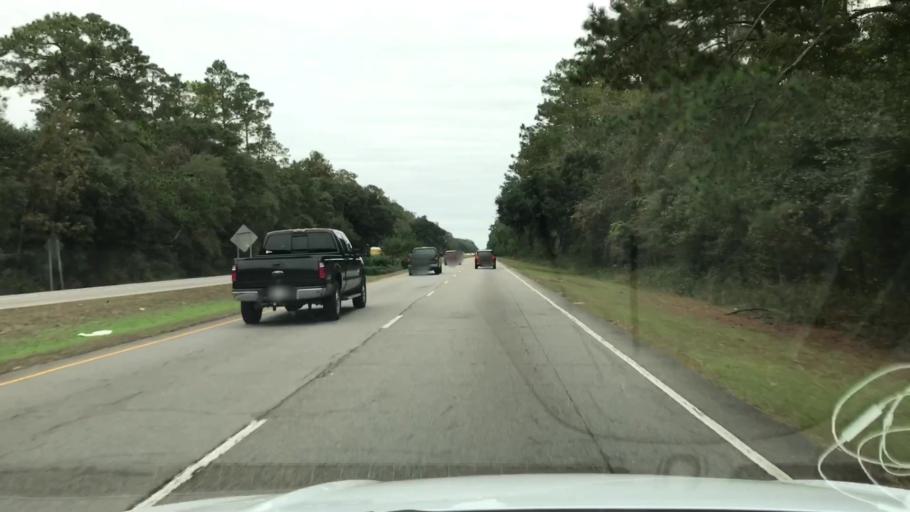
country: US
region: South Carolina
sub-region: Georgetown County
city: Murrells Inlet
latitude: 33.5008
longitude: -79.0826
